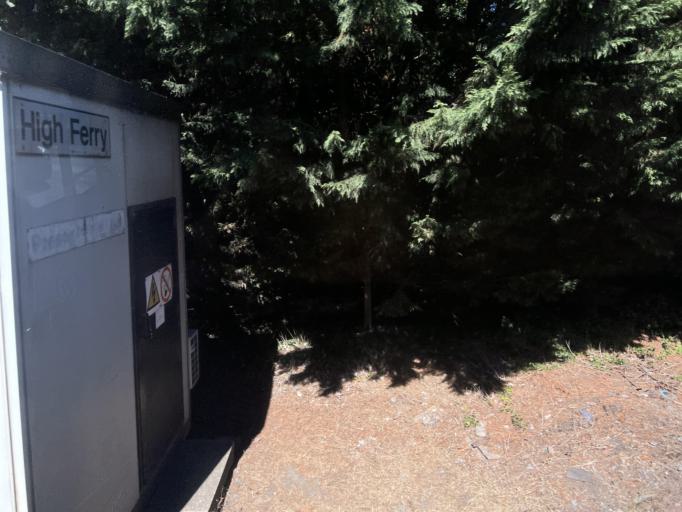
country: GB
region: England
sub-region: Lincolnshire
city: Boston
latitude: 53.0257
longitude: 0.0144
